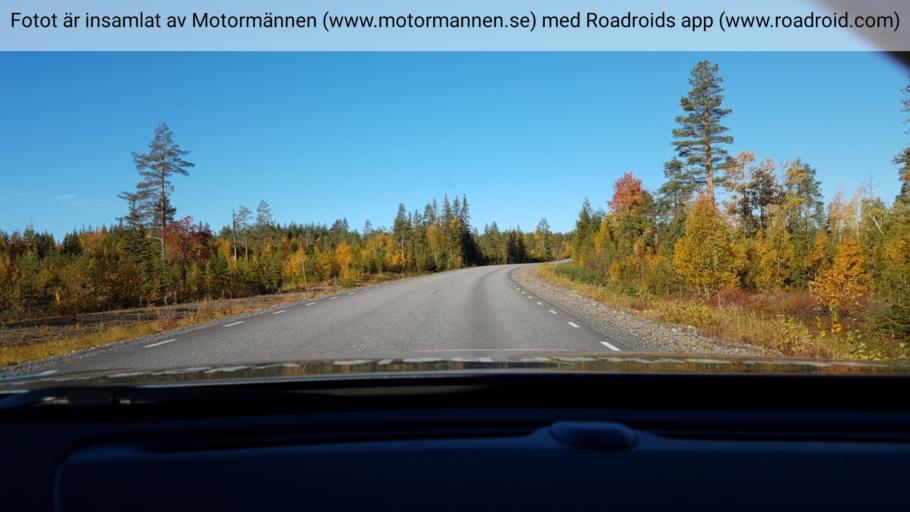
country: SE
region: Vaesterbotten
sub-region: Skelleftea Kommun
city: Storvik
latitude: 65.3237
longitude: 20.7744
